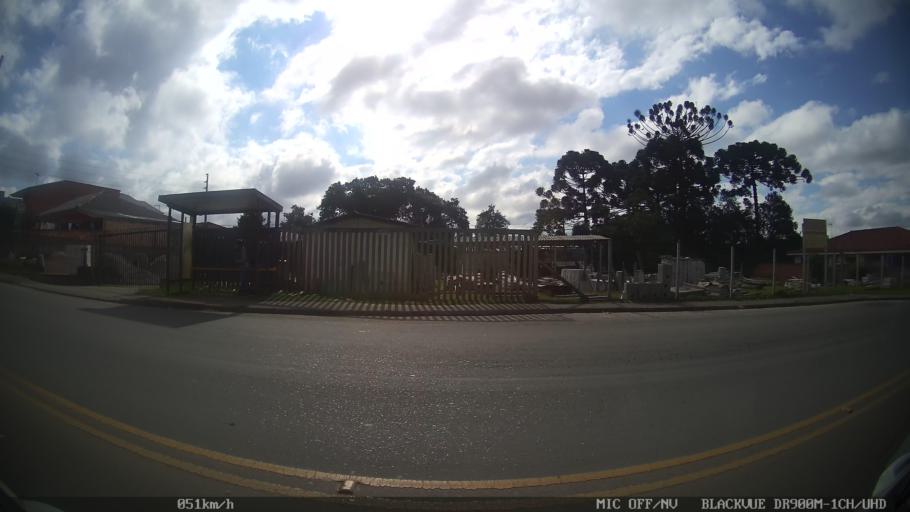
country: BR
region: Parana
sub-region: Colombo
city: Colombo
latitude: -25.3452
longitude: -49.1908
